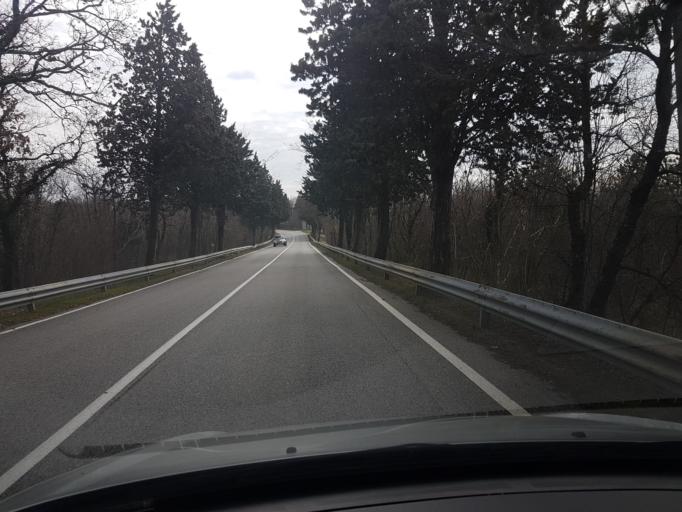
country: IT
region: Friuli Venezia Giulia
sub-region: Provincia di Trieste
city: Aurisina
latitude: 45.7569
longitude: 13.6888
